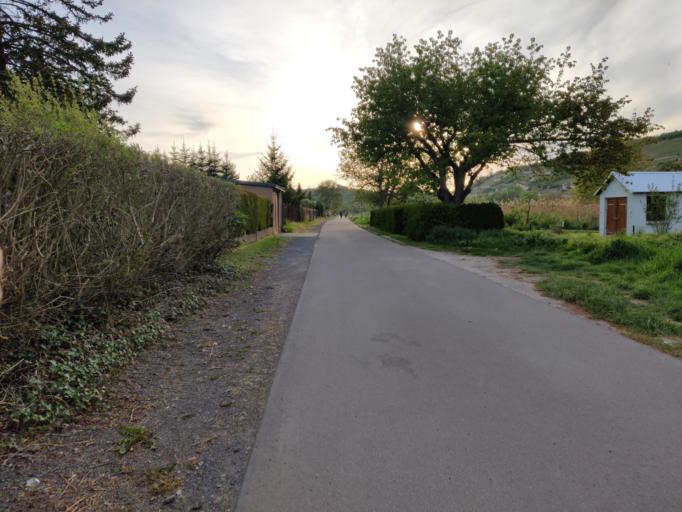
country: DE
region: Saxony-Anhalt
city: Freyburg
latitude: 51.2111
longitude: 11.7607
